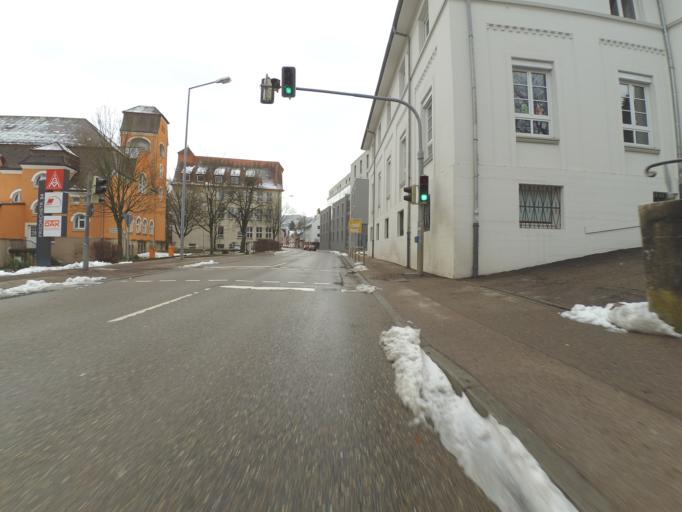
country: DE
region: Baden-Wuerttemberg
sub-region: Regierungsbezirk Stuttgart
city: Aalen
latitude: 48.8397
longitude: 10.0888
